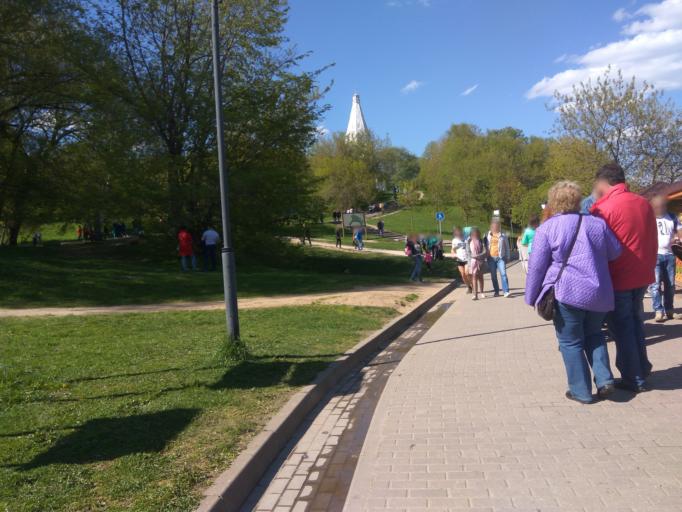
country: RU
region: Moscow
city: Kolomenskoye
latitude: 55.6647
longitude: 37.6717
